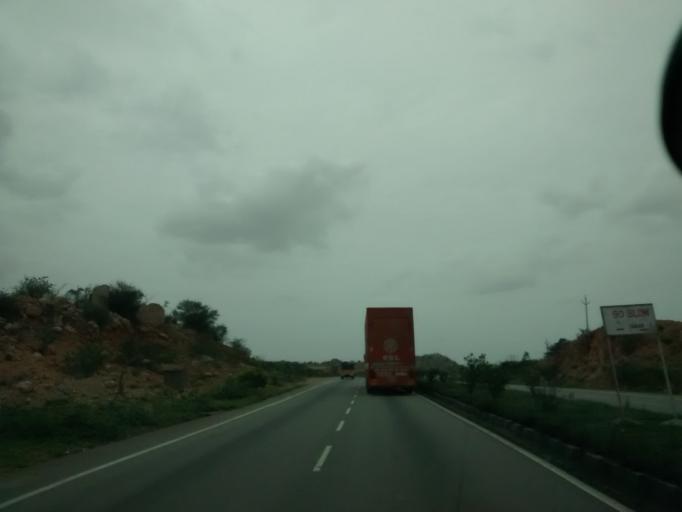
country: IN
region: Andhra Pradesh
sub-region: Kurnool
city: Ramapuram
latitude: 15.2012
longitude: 77.7129
